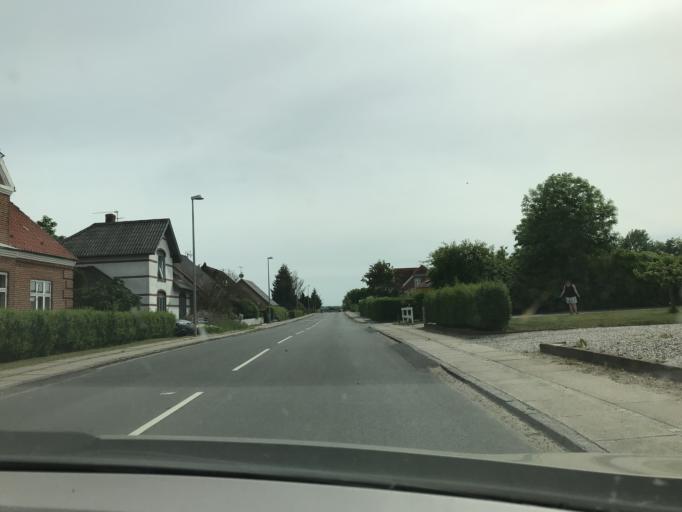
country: DK
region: Central Jutland
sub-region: Norddjurs Kommune
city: Allingabro
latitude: 56.4984
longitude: 10.3315
